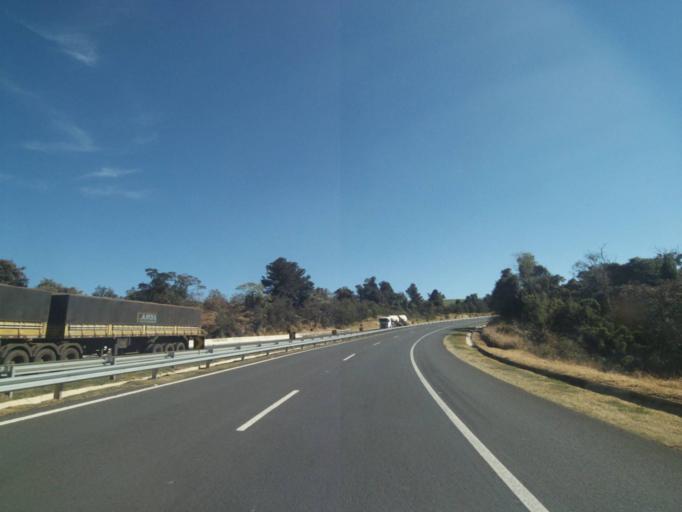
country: BR
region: Parana
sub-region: Tibagi
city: Tibagi
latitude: -24.8499
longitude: -50.4711
